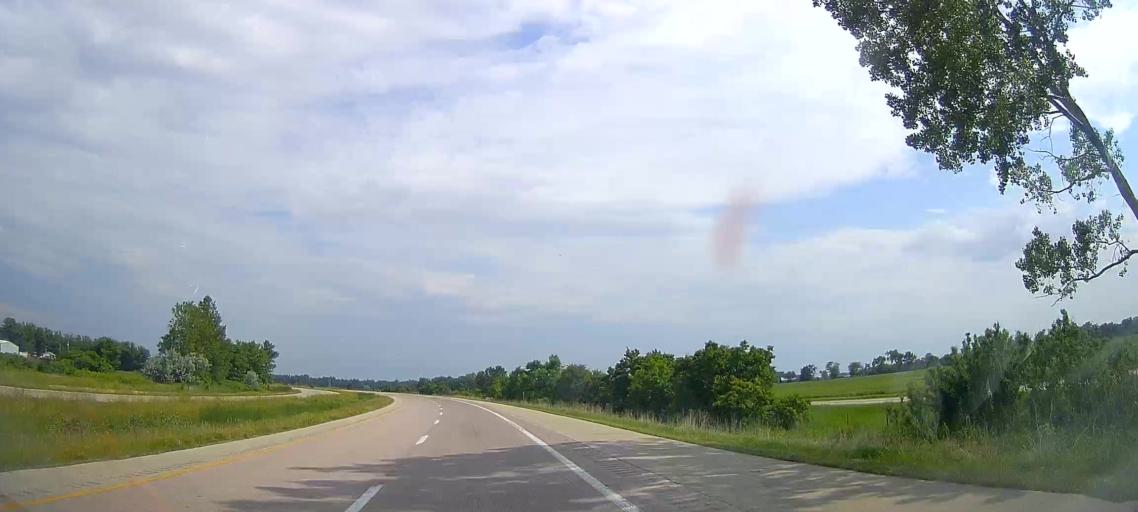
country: US
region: Nebraska
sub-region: Burt County
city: Tekamah
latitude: 41.8537
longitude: -96.1019
